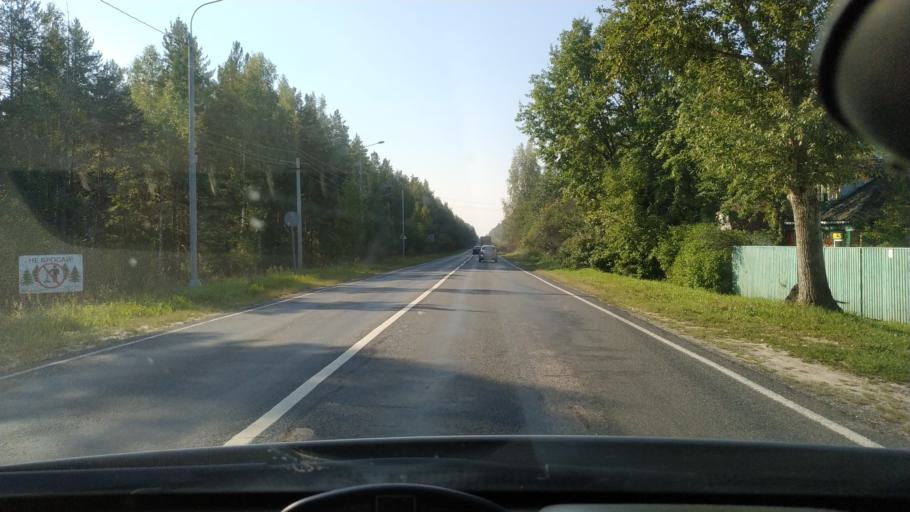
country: RU
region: Moskovskaya
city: Tugolesskiy Bor
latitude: 55.5172
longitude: 39.7116
